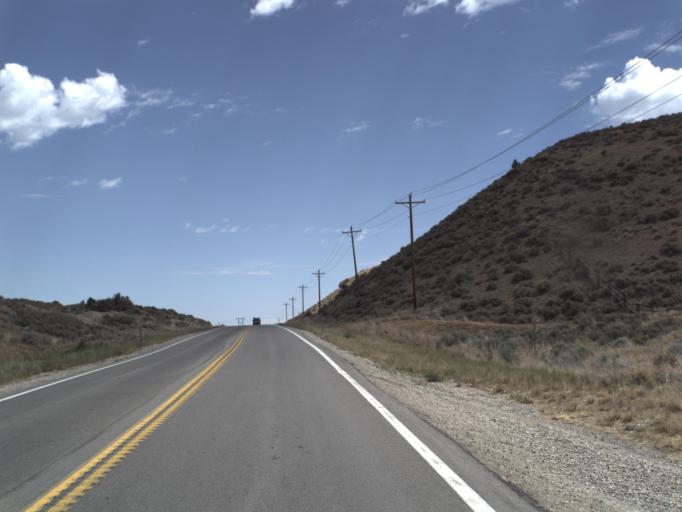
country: US
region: Utah
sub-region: Tooele County
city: Tooele
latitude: 40.4641
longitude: -112.3544
